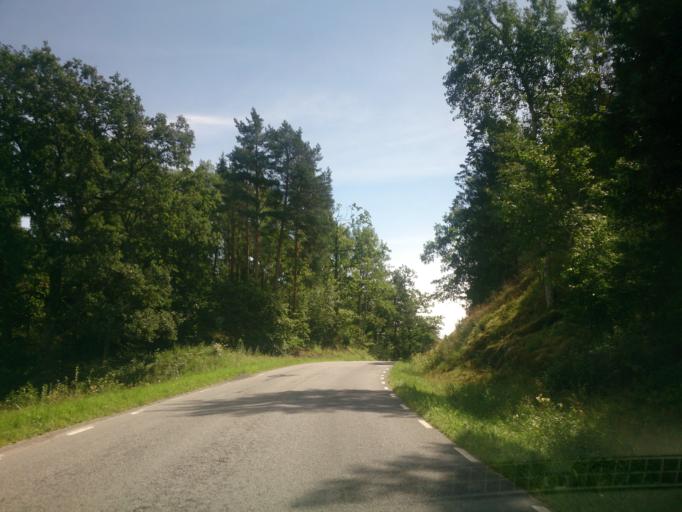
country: SE
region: OEstergoetland
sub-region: Valdemarsviks Kommun
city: Valdemarsvik
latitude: 58.2780
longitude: 16.7066
